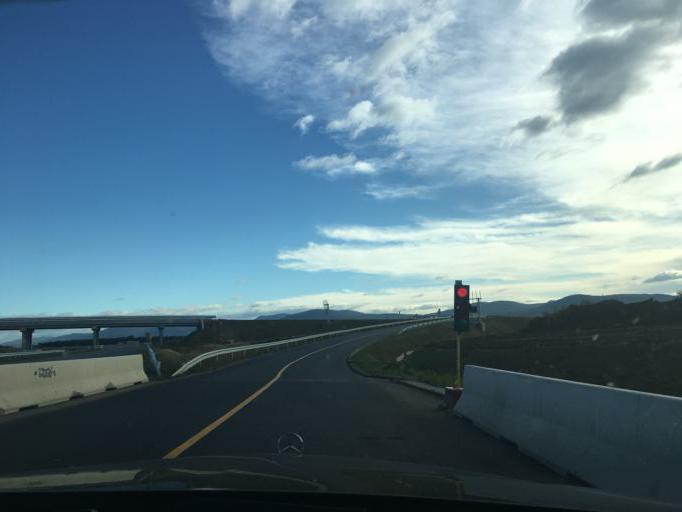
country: HU
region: Borsod-Abauj-Zemplen
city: Gonc
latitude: 48.5243
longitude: 21.2464
